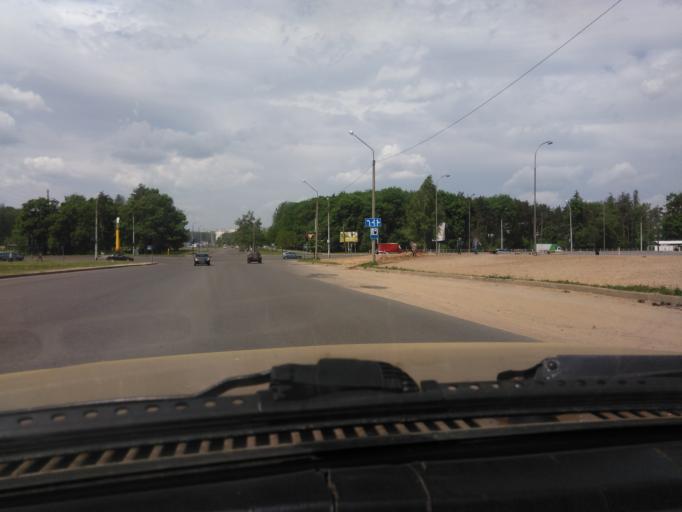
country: BY
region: Mogilev
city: Mahilyow
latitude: 53.9464
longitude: 30.3583
